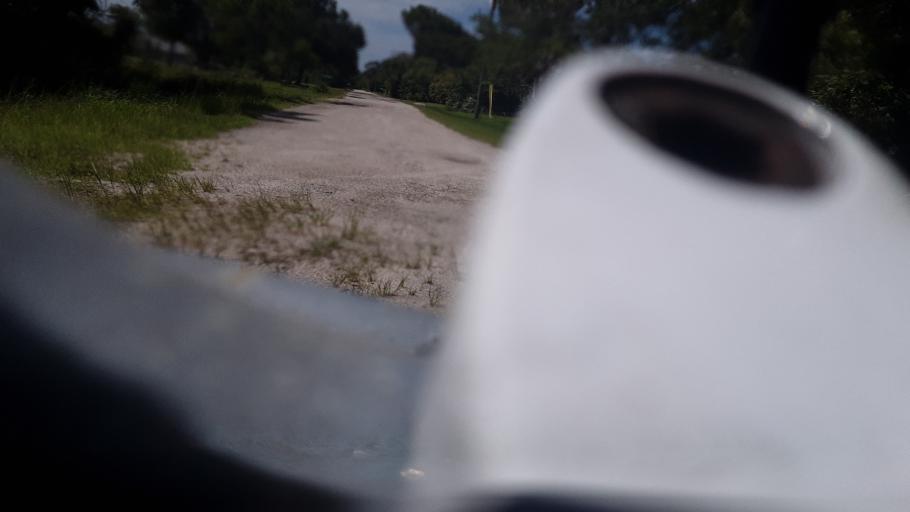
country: US
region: Florida
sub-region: Brevard County
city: Malabar
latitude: 27.9882
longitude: -80.6100
